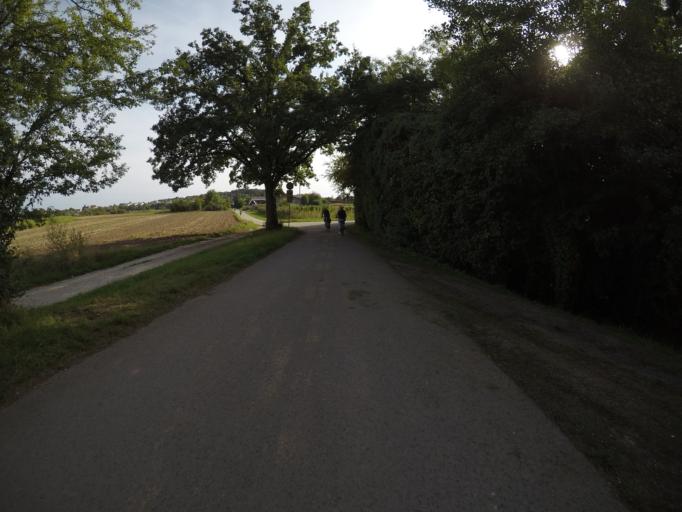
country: DE
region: Baden-Wuerttemberg
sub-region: Regierungsbezirk Stuttgart
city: Leinfelden-Echterdingen
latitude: 48.7080
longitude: 9.1306
